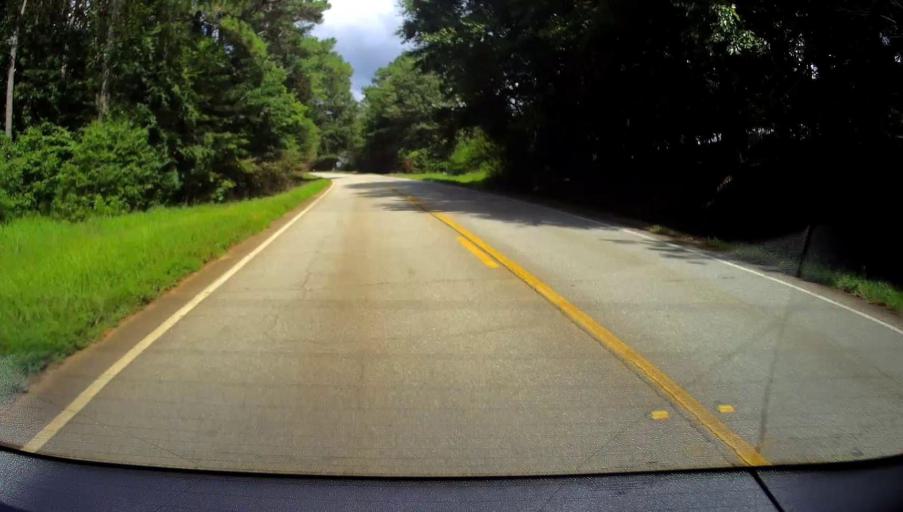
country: US
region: Georgia
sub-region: Crawford County
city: Knoxville
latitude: 32.8820
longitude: -84.0137
